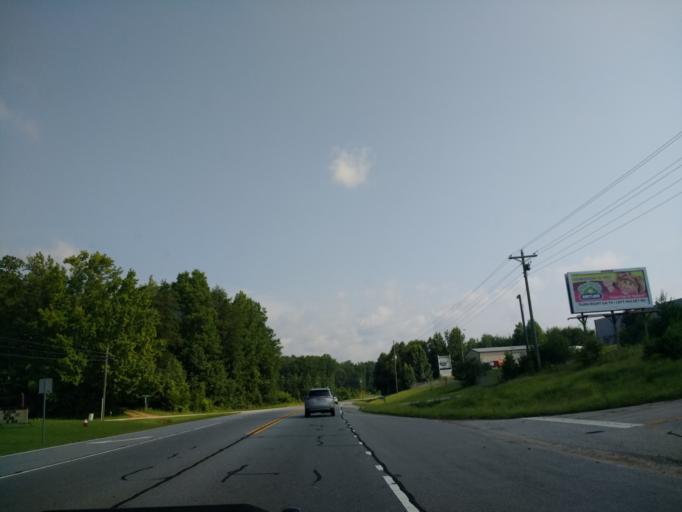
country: US
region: Georgia
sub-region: White County
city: Cleveland
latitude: 34.5616
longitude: -83.7631
